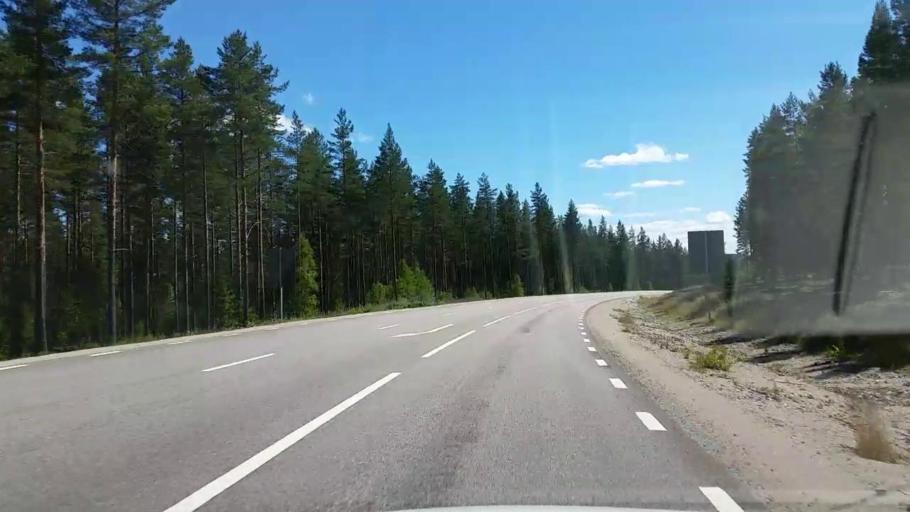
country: SE
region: Gaevleborg
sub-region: Bollnas Kommun
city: Vittsjo
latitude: 61.0600
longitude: 15.8030
